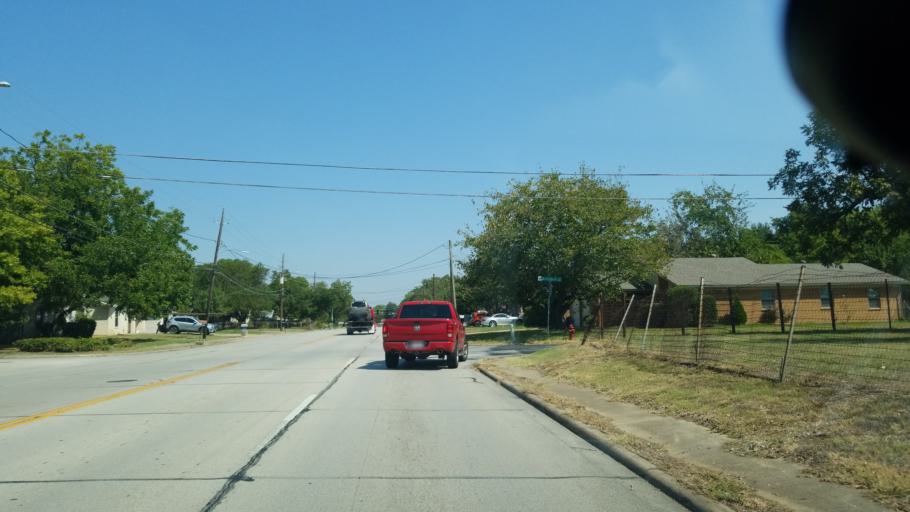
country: US
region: Texas
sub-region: Dallas County
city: Grand Prairie
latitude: 32.7076
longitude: -96.9856
